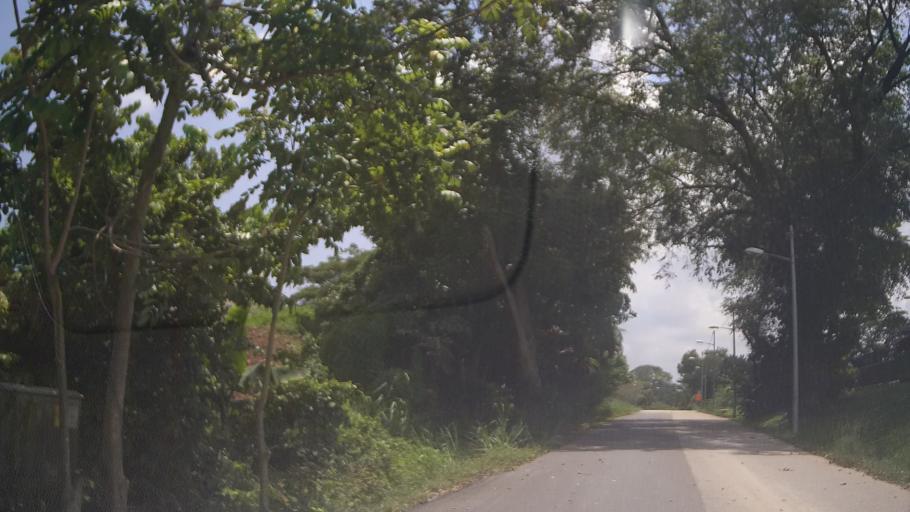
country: MY
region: Johor
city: Kampung Pasir Gudang Baru
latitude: 1.3978
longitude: 103.8626
